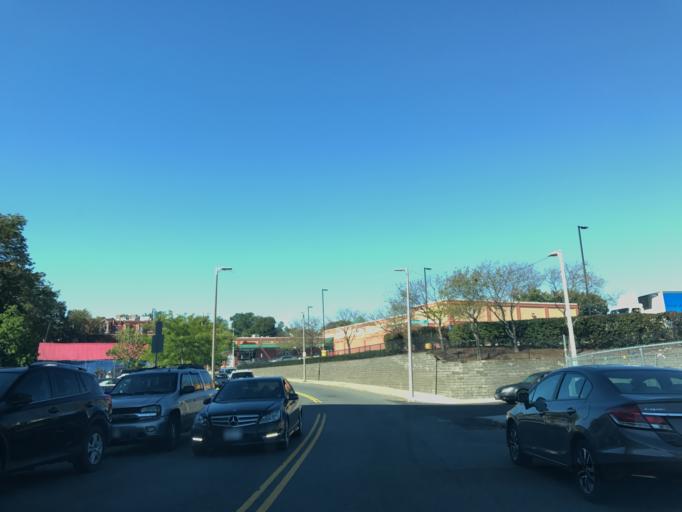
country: US
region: Massachusetts
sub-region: Suffolk County
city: Jamaica Plain
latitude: 42.3079
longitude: -71.0809
